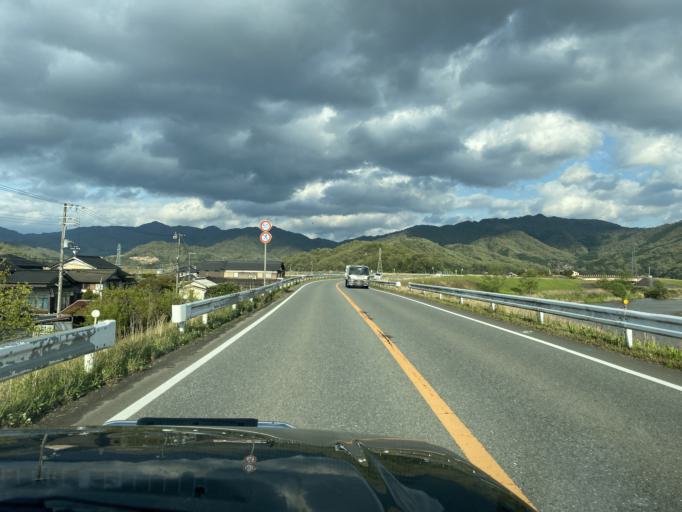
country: JP
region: Hyogo
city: Toyooka
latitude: 35.4888
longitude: 134.8522
